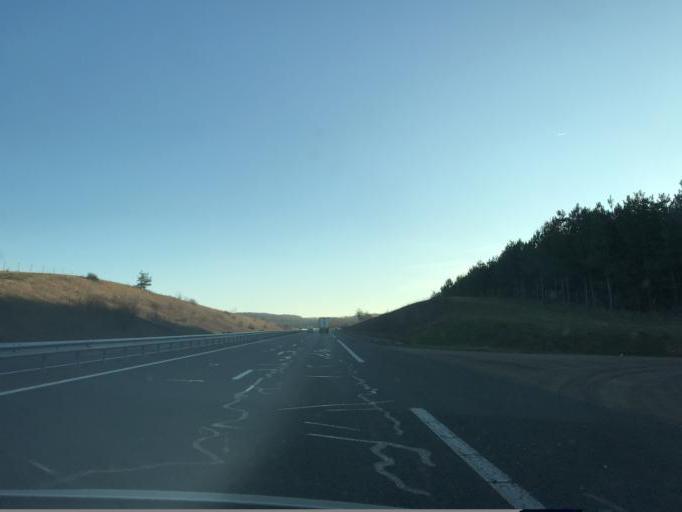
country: FR
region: Bourgogne
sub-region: Departement de l'Yonne
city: Saint-Martin-du-Tertre
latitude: 48.2223
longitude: 3.2382
